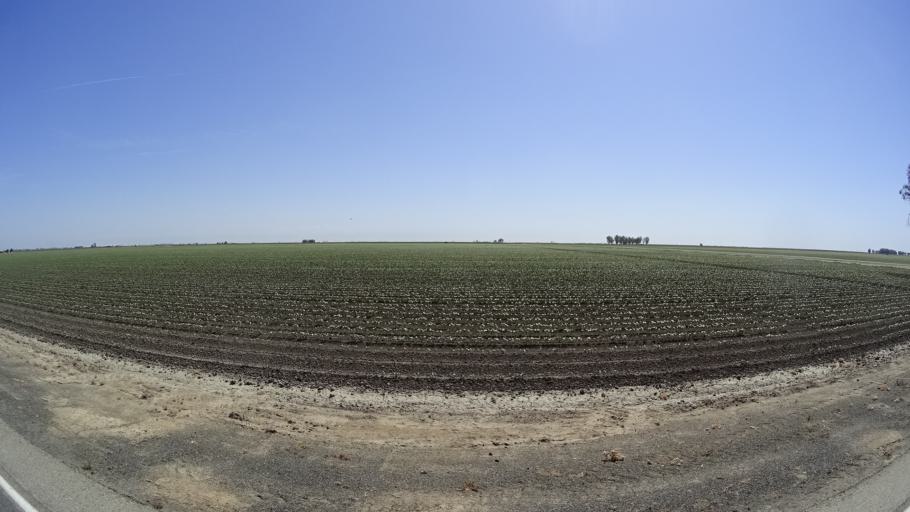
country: US
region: California
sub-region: Kings County
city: Stratford
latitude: 36.1901
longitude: -119.7803
